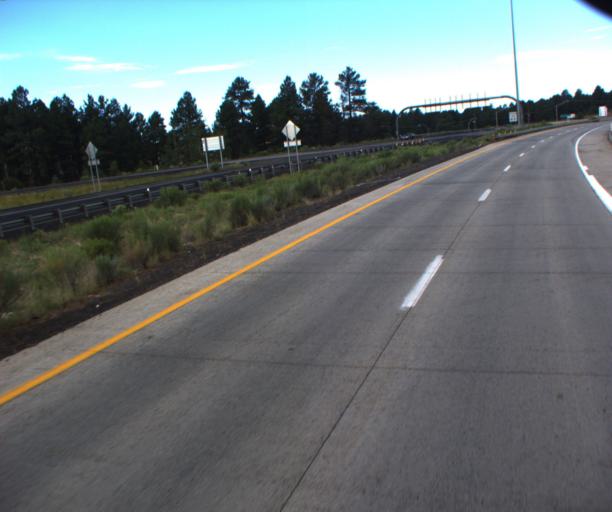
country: US
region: Arizona
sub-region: Coconino County
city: Flagstaff
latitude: 35.1704
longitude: -111.6635
